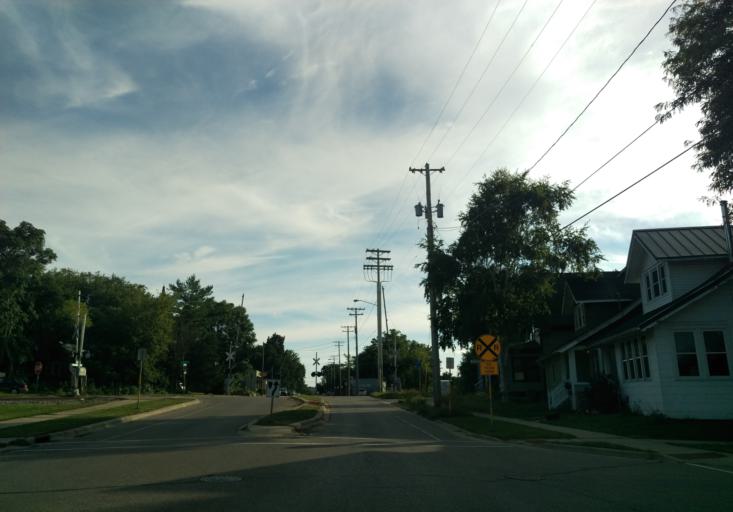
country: US
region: Wisconsin
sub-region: Dane County
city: Maple Bluff
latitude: 43.0974
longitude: -89.3510
